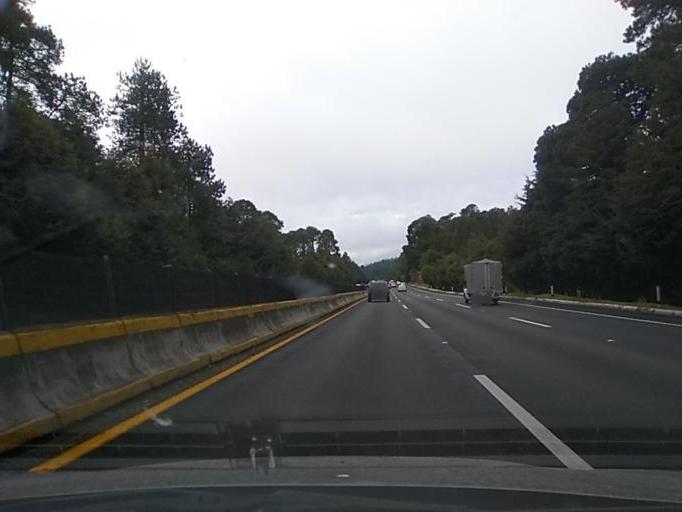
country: MX
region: Morelos
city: Tres Marias
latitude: 19.1070
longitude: -99.1888
